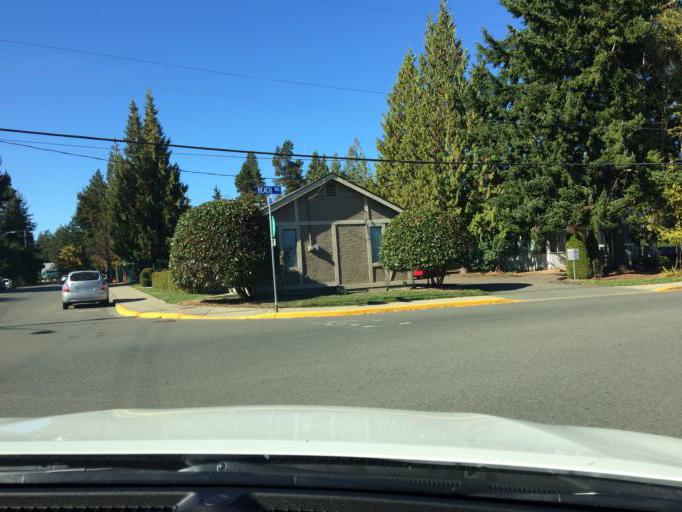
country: CA
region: British Columbia
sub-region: Regional District of Nanaimo
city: Parksville
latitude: 49.3462
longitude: -124.4469
